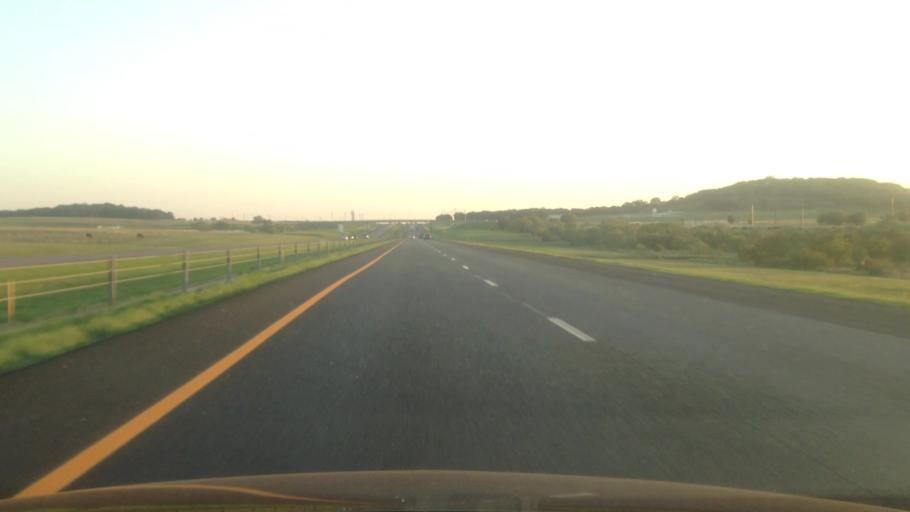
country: US
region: Texas
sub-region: Denton County
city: Argyle
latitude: 33.1591
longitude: -97.1890
